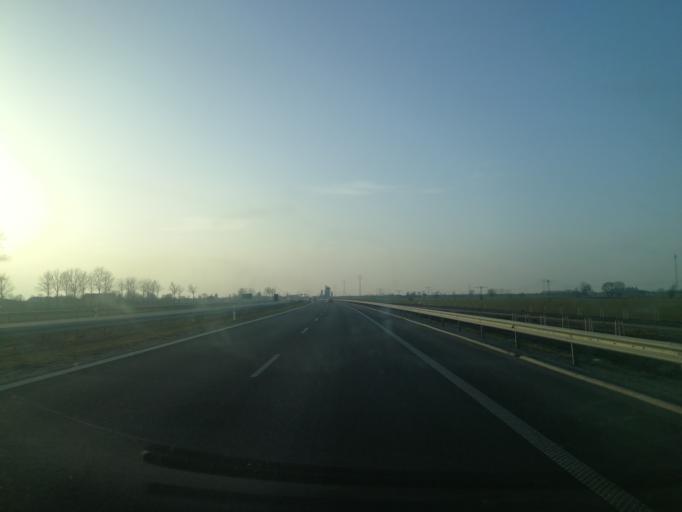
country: PL
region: Pomeranian Voivodeship
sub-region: Powiat nowodworski
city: Ostaszewo
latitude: 54.2531
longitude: 18.9753
